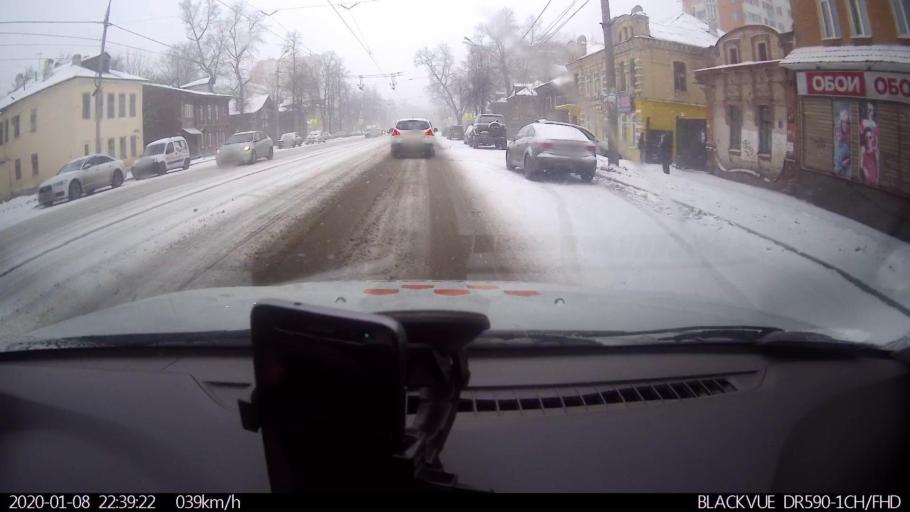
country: RU
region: Nizjnij Novgorod
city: Nizhniy Novgorod
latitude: 56.3157
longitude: 43.9399
